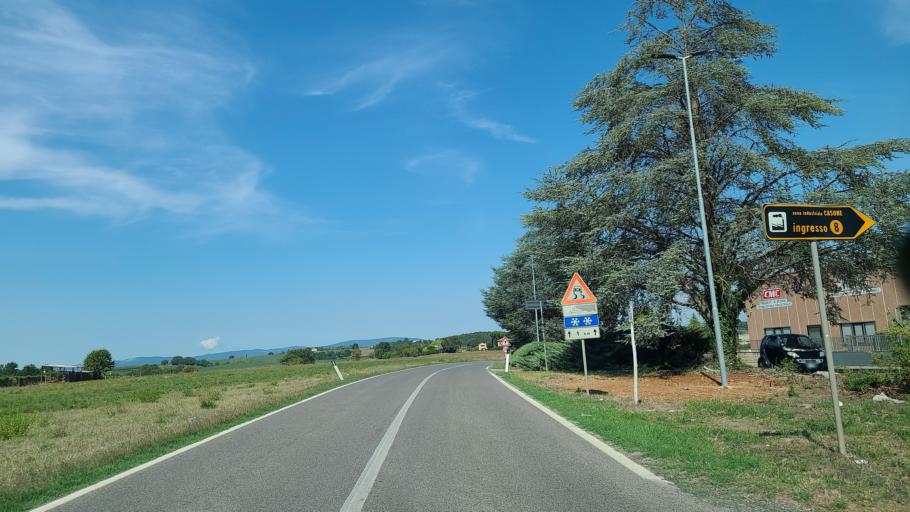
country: IT
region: Tuscany
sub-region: Provincia di Siena
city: Staggia
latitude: 43.3965
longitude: 11.1798
